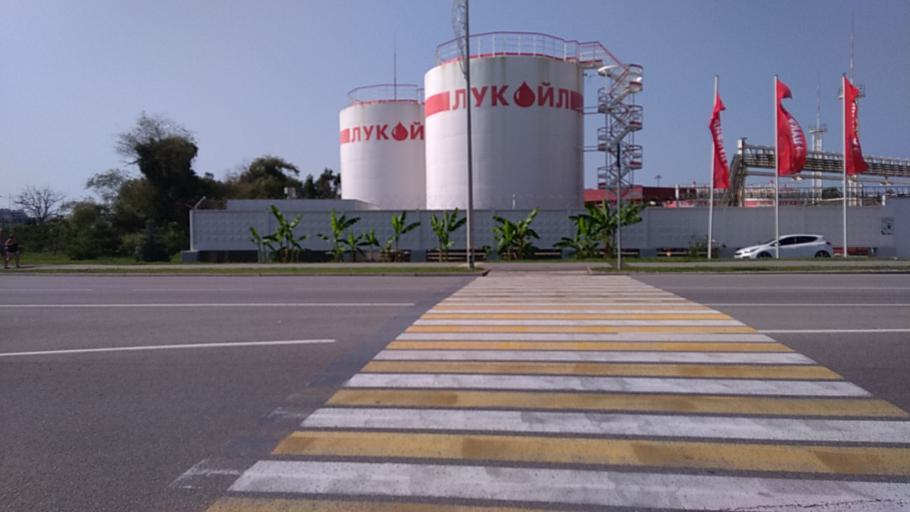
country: RU
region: Krasnodarskiy
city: Vysokoye
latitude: 43.3959
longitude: 39.9910
